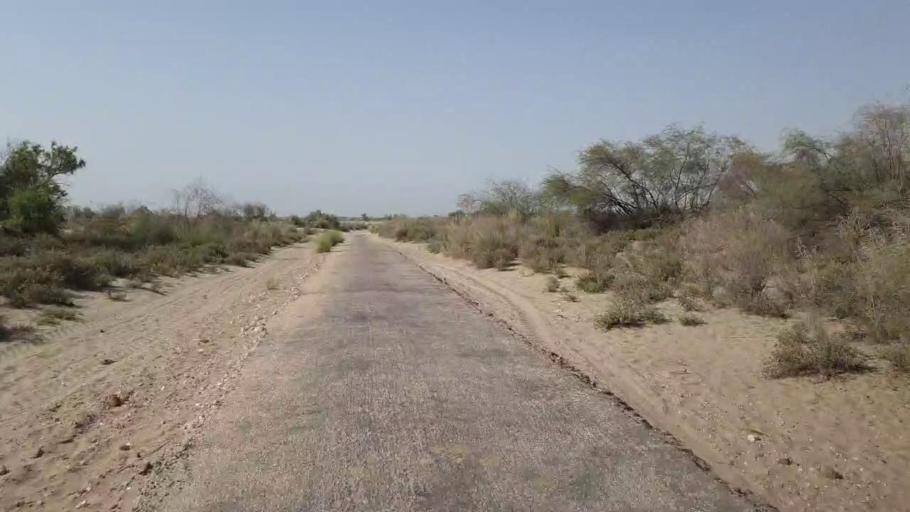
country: PK
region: Sindh
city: Jam Sahib
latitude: 26.5955
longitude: 68.9229
